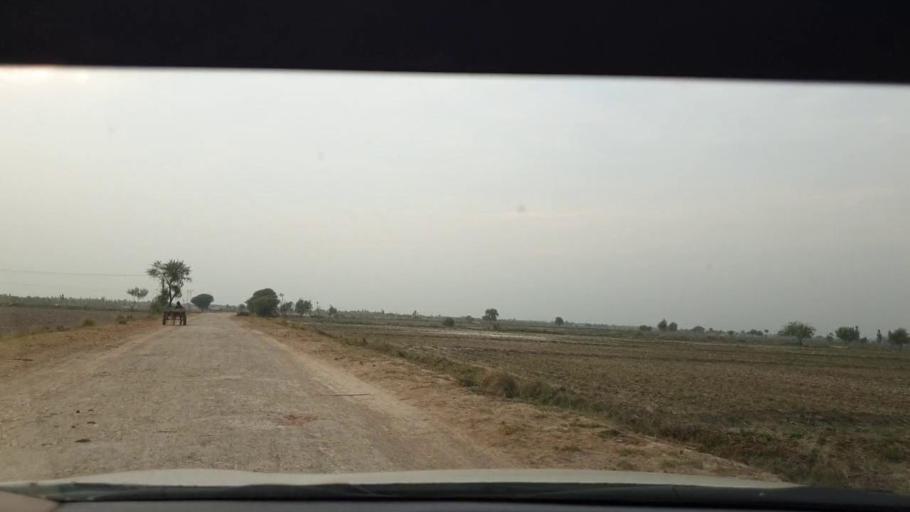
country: PK
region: Sindh
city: Sinjhoro
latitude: 25.9134
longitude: 68.7628
